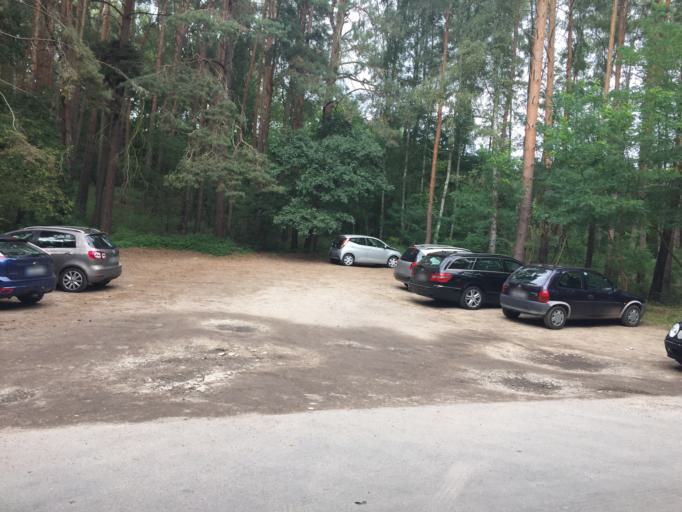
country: DE
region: Brandenburg
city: Belzig
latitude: 52.1645
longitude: 12.6062
